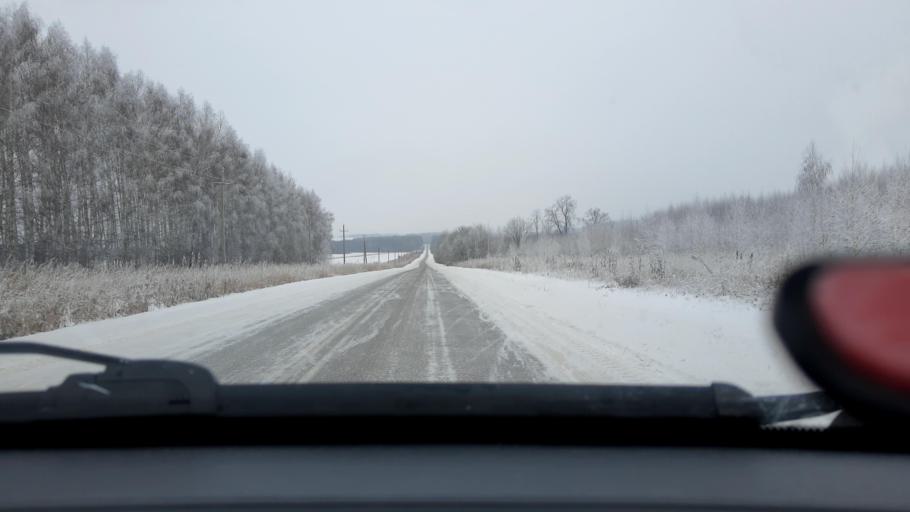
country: RU
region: Bashkortostan
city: Iglino
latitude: 54.6603
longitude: 56.4239
